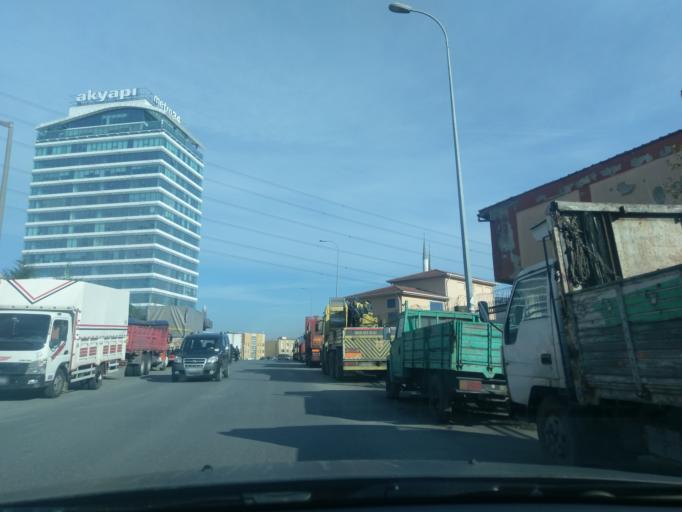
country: TR
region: Istanbul
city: Basaksehir
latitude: 41.0683
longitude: 28.8032
